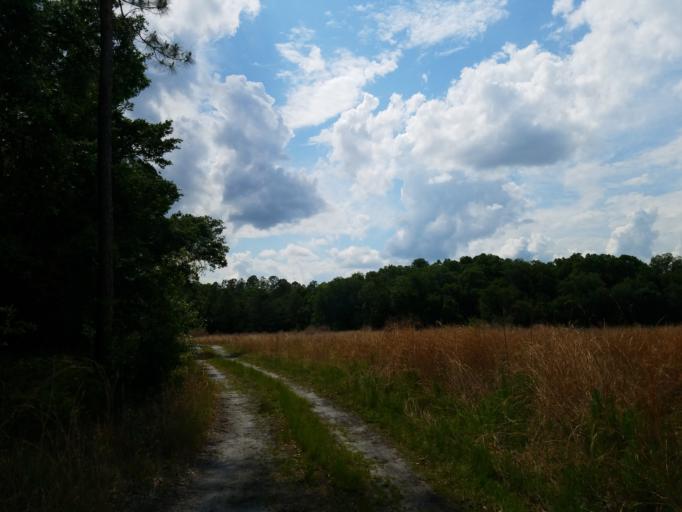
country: US
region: Florida
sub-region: Hernando County
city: Hill 'n Dale
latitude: 28.5509
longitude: -82.2582
